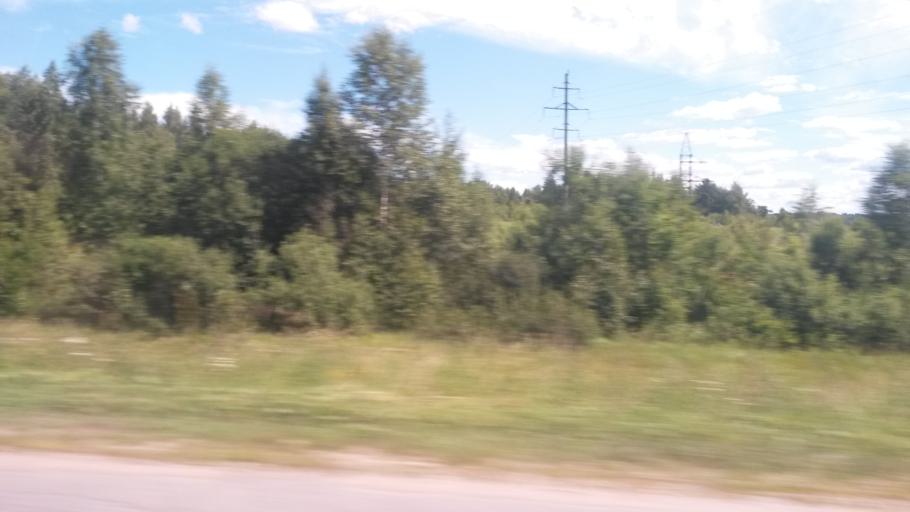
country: RU
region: Ivanovo
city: Rodniki
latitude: 57.1074
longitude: 41.7790
